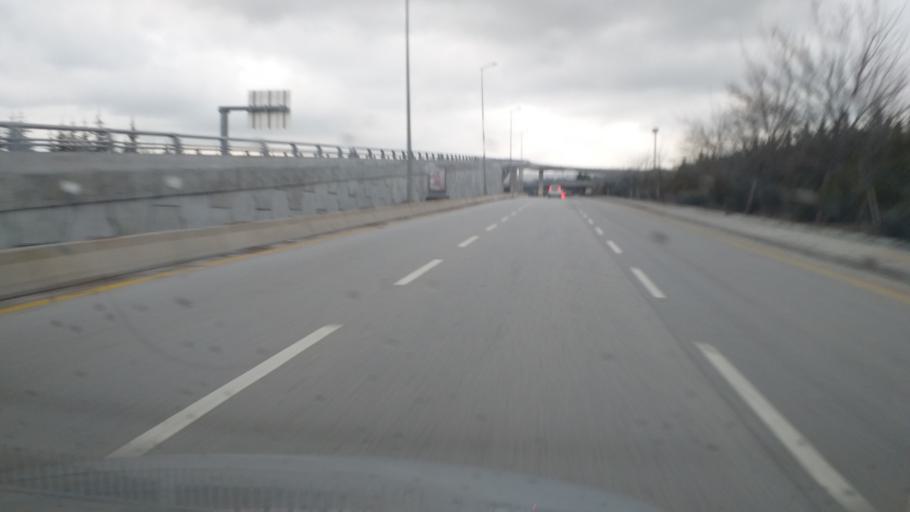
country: TR
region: Ankara
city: Batikent
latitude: 39.8998
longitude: 32.7332
